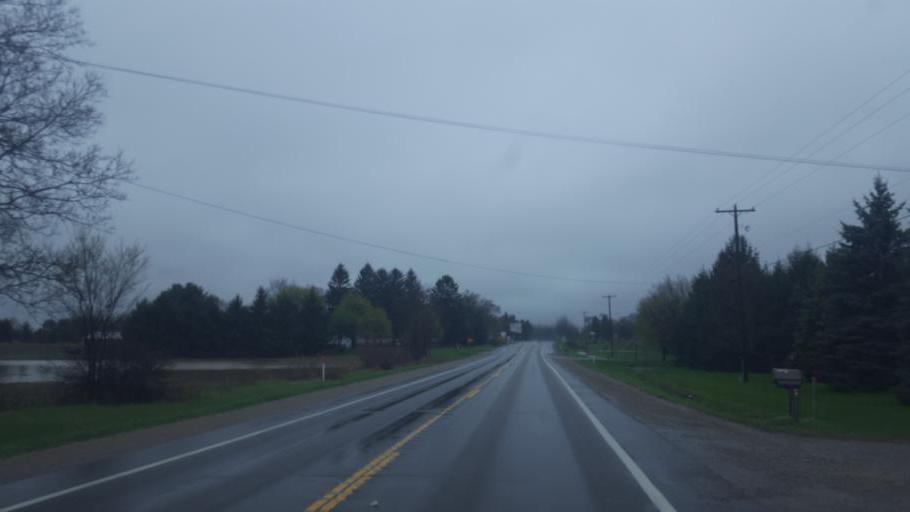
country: US
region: Michigan
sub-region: Isabella County
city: Mount Pleasant
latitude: 43.5967
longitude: -84.8431
